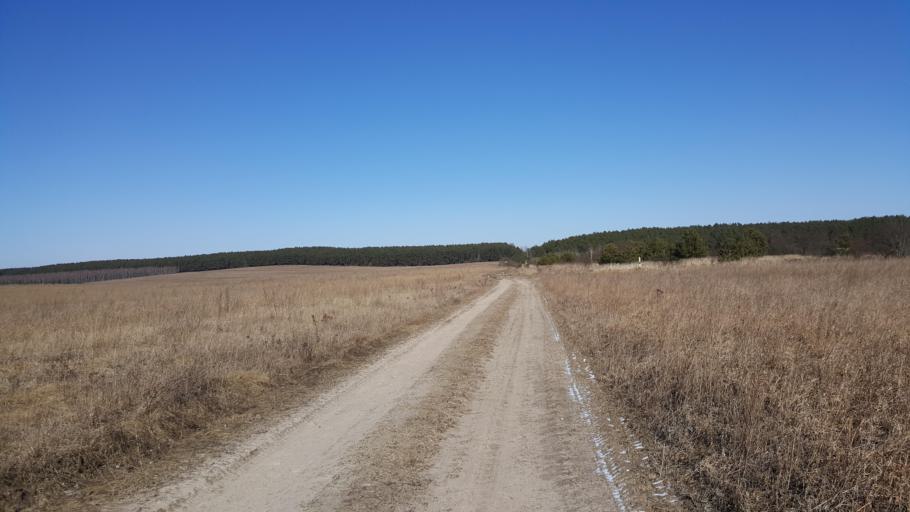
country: BY
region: Brest
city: Kamyanyets
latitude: 52.3730
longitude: 23.8357
